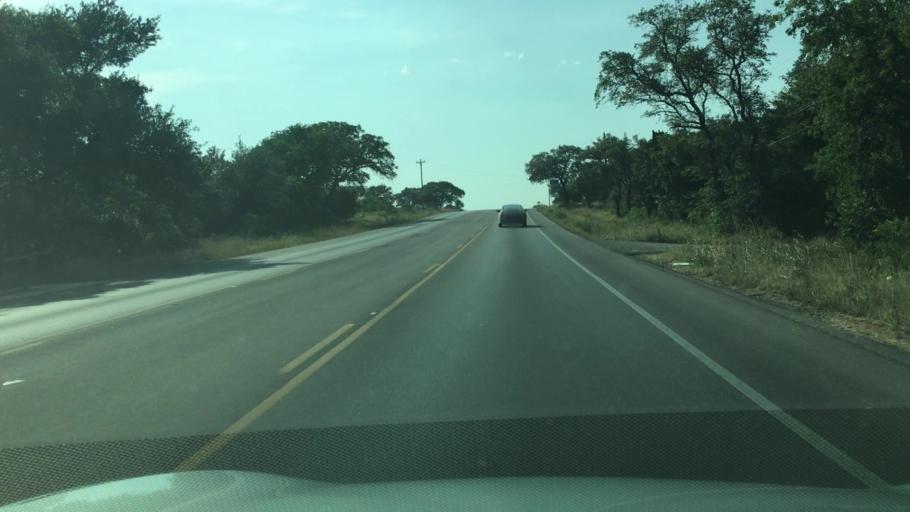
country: US
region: Texas
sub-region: Hays County
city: Wimberley
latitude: 29.9248
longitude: -98.0639
